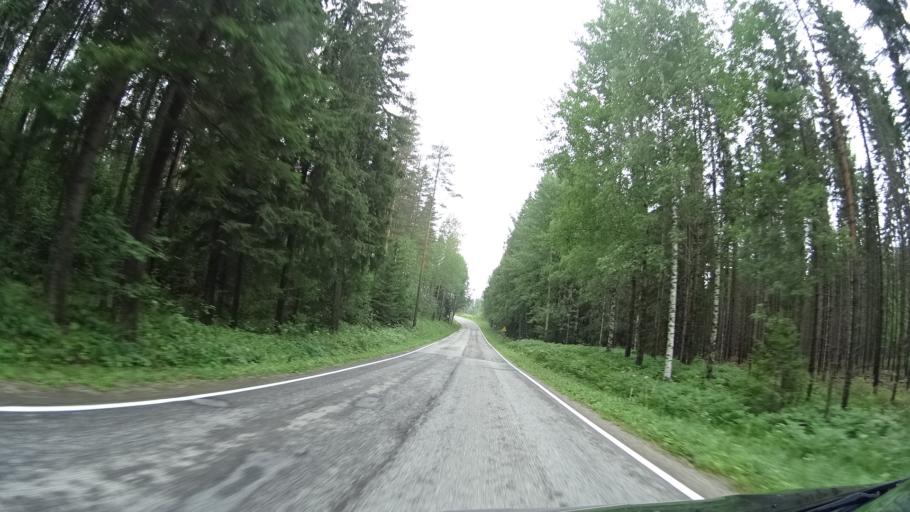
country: FI
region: Southern Savonia
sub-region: Savonlinna
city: Punkaharju
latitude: 61.7547
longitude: 29.4556
